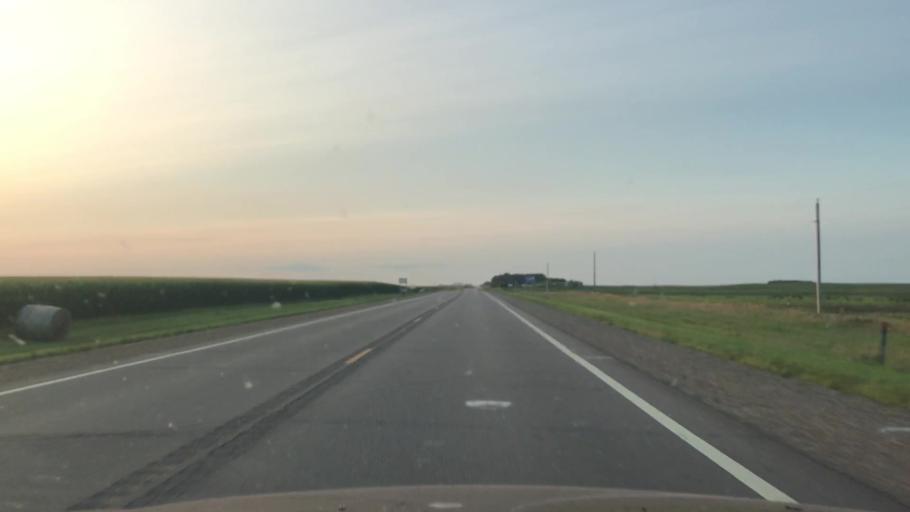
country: US
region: Minnesota
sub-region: Redwood County
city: Redwood Falls
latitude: 44.4348
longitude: -95.1176
